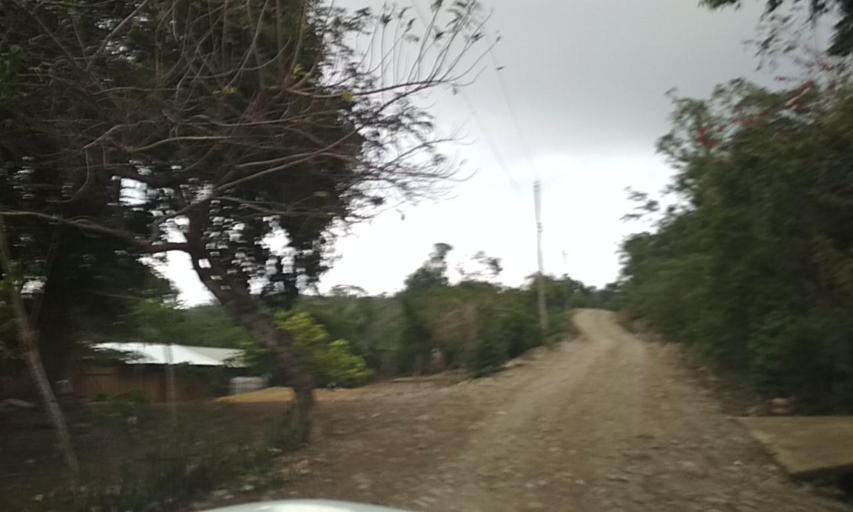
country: MX
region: Veracruz
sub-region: Coatzintla
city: Manuel Maria Contreras
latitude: 20.3797
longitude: -97.4447
